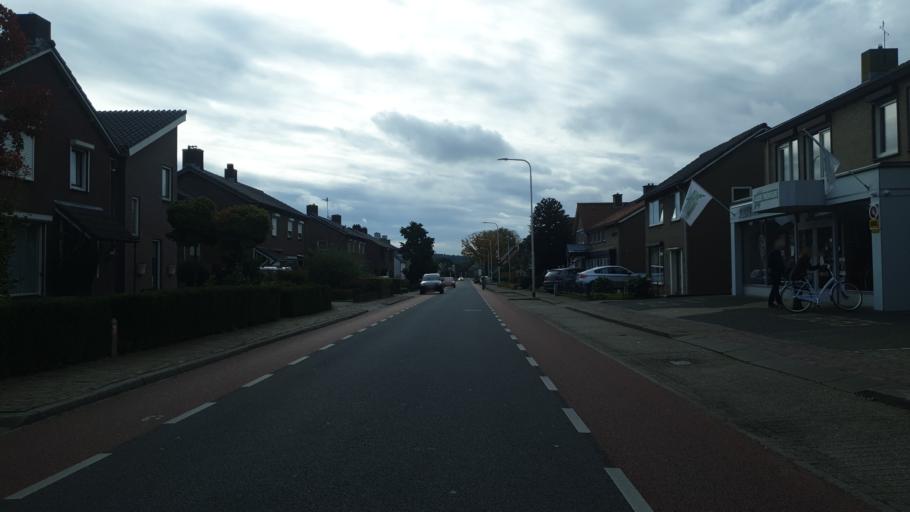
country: NL
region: Gelderland
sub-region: Gemeente Groesbeek
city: Bredeweg
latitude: 51.7612
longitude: 5.9413
